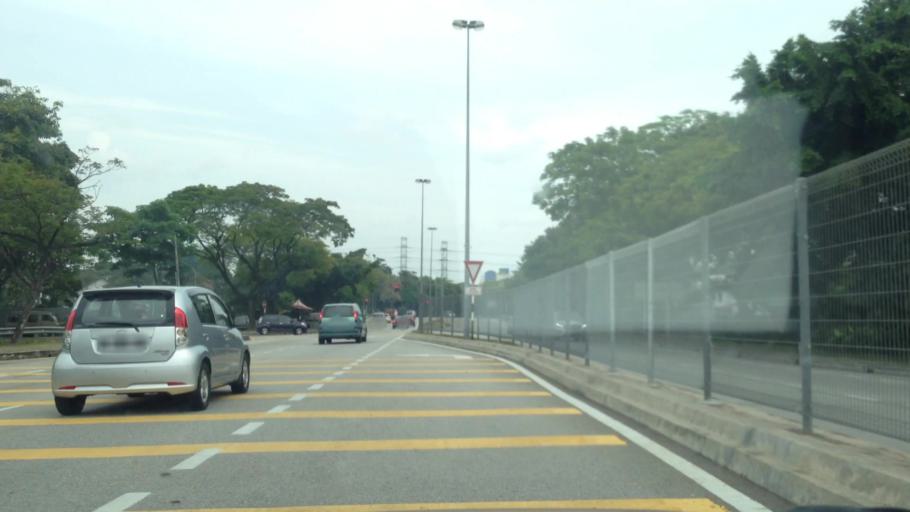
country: MY
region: Selangor
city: Subang Jaya
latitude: 3.0449
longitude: 101.5738
